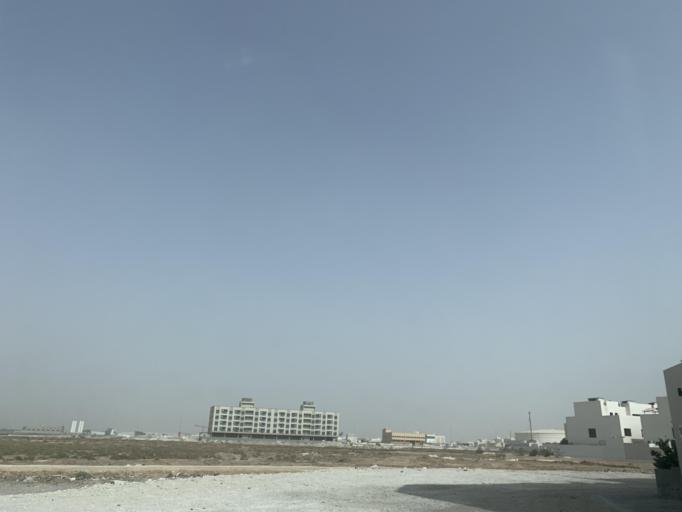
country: BH
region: Northern
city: Madinat `Isa
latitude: 26.1892
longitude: 50.5141
